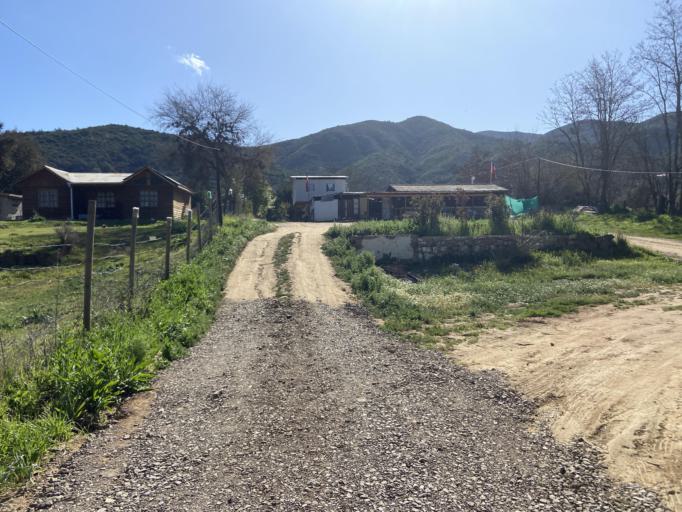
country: CL
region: Valparaiso
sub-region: Provincia de Marga Marga
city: Limache
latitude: -33.1737
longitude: -71.1667
